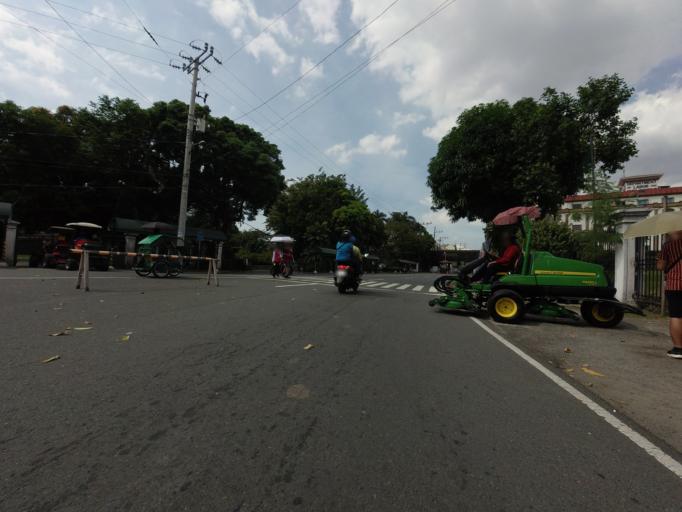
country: PH
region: Metro Manila
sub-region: City of Manila
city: Port Area
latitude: 14.5859
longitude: 120.9784
